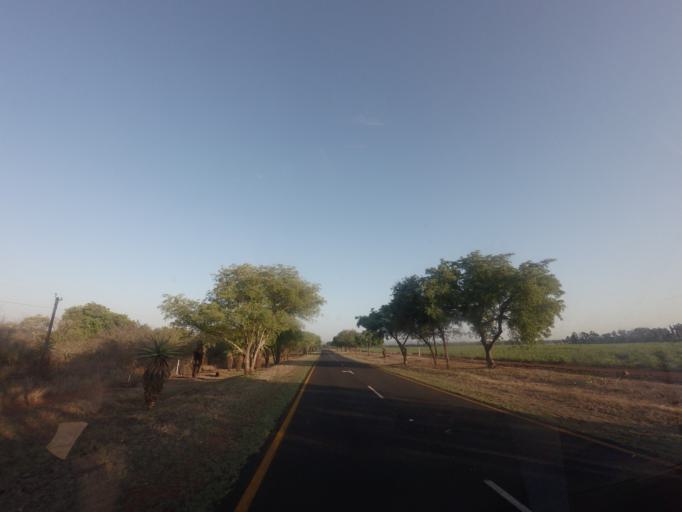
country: ZA
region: Mpumalanga
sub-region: Ehlanzeni District
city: Komatipoort
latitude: -25.3704
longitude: 31.9036
